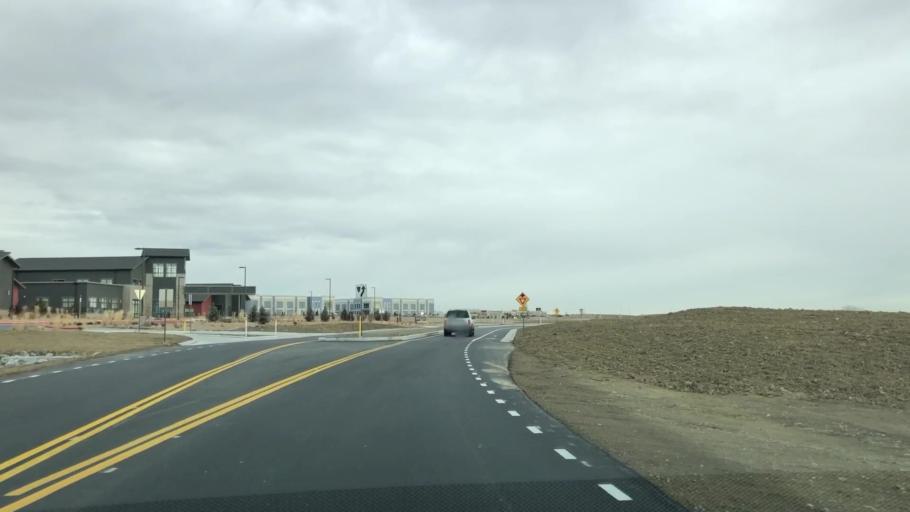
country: US
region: Colorado
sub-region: Larimer County
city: Loveland
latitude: 40.4290
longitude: -105.0121
